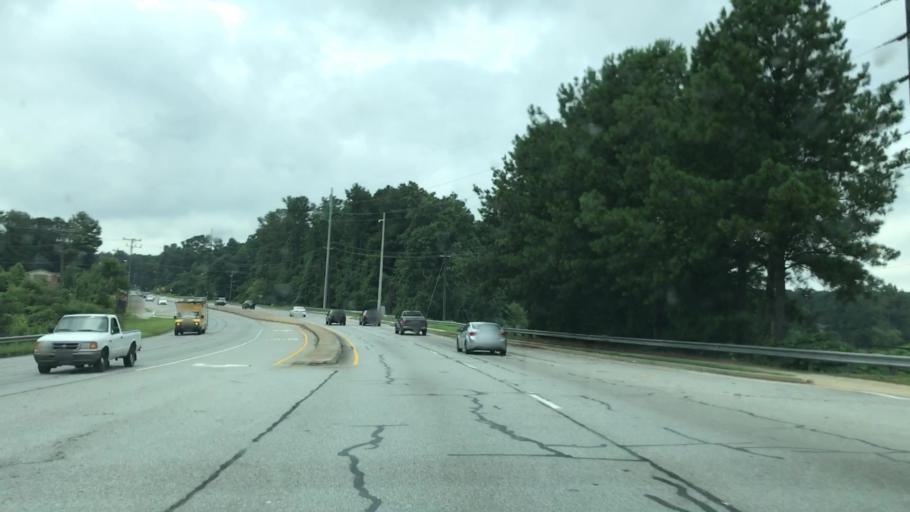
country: US
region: Georgia
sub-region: Gwinnett County
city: Lilburn
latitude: 33.9212
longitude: -84.1391
